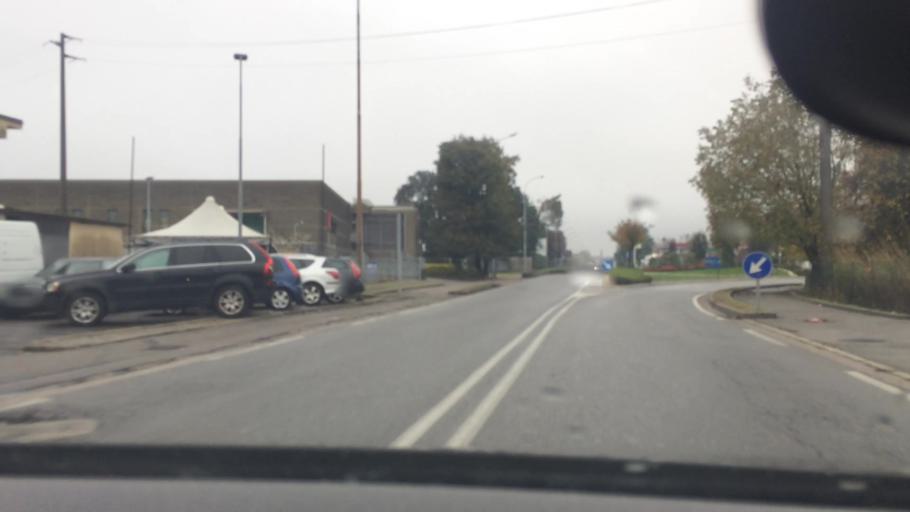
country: IT
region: Lombardy
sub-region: Provincia di Como
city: Mariano Comense
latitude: 45.7093
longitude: 9.1688
